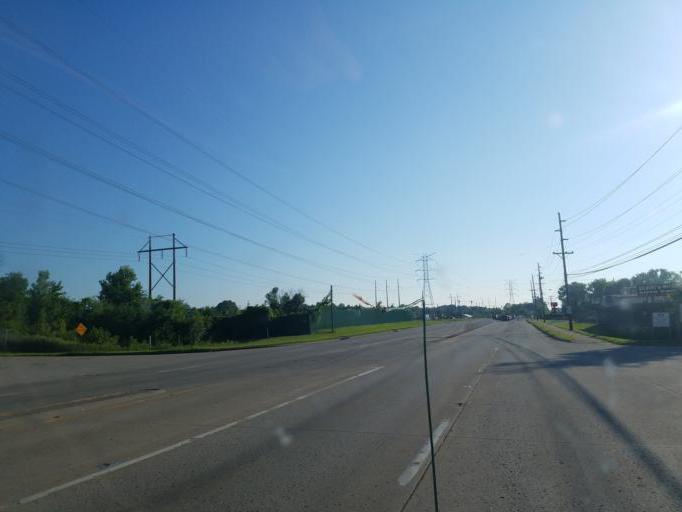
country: US
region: Kentucky
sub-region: Jefferson County
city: Fairdale
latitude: 38.1277
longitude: -85.7459
